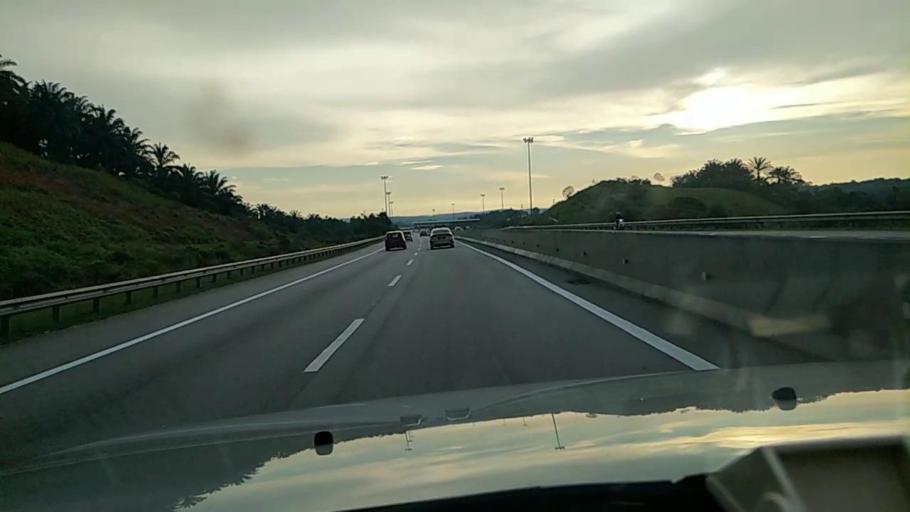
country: MY
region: Selangor
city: Kuang
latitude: 3.2714
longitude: 101.5361
